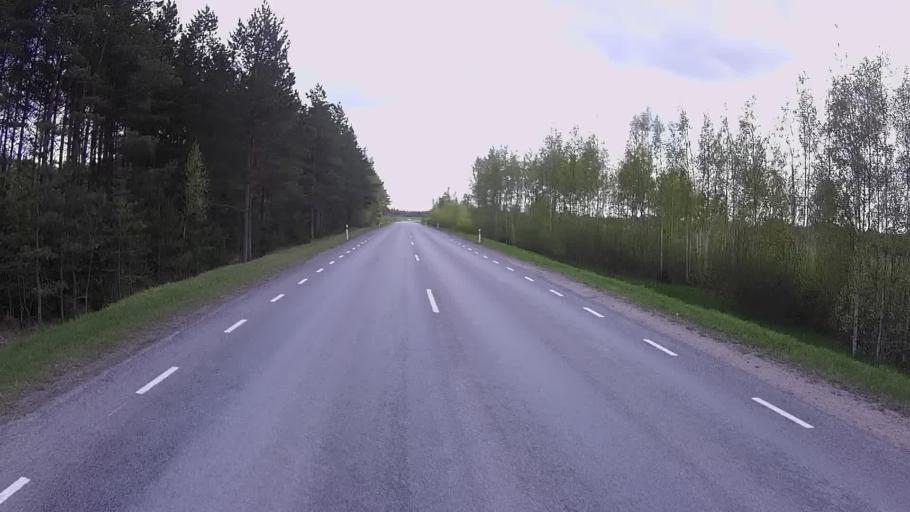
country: EE
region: Tartu
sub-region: Alatskivi vald
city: Kallaste
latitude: 58.5214
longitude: 27.0037
